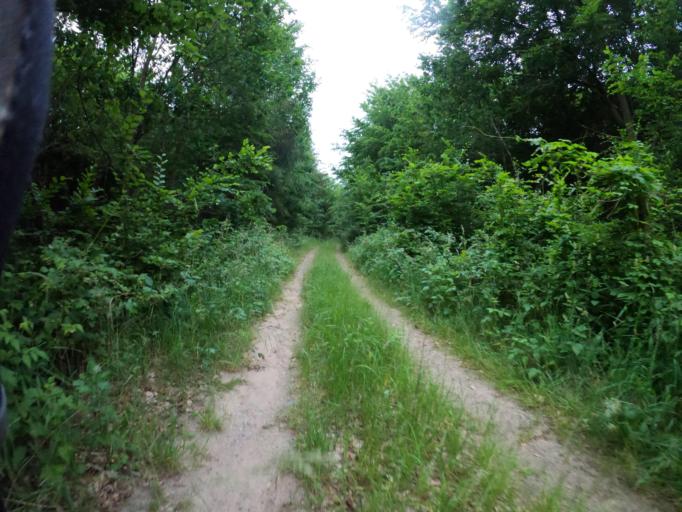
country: PL
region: West Pomeranian Voivodeship
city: Trzcinsko Zdroj
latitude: 52.9132
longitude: 14.7276
